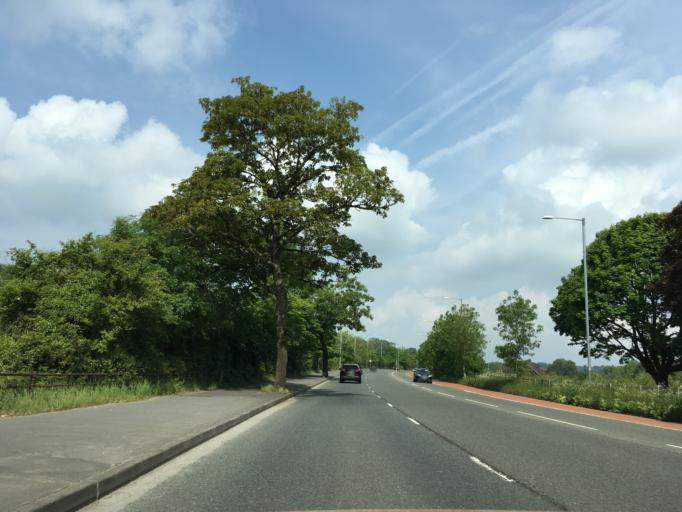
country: GB
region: England
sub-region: North Somerset
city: Long Ashton
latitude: 51.4718
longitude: -2.6447
